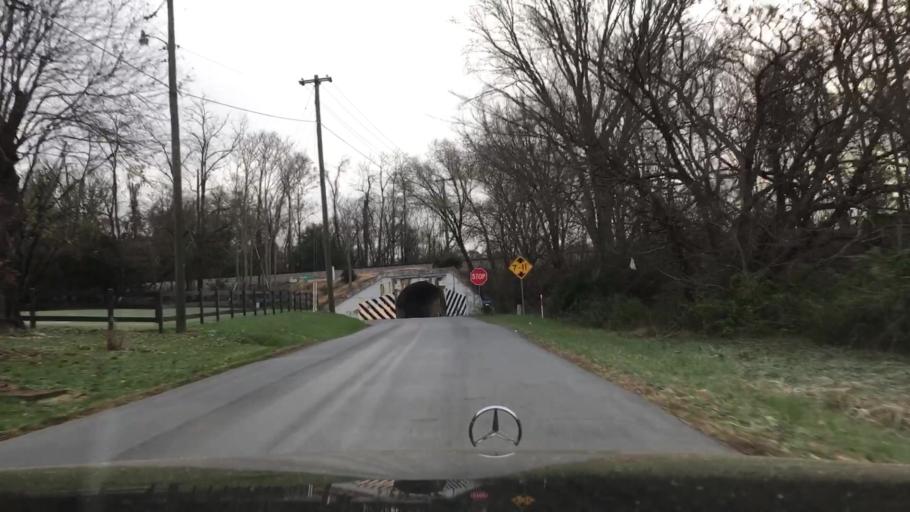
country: US
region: Virginia
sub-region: Campbell County
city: Altavista
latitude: 37.1461
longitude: -79.3017
